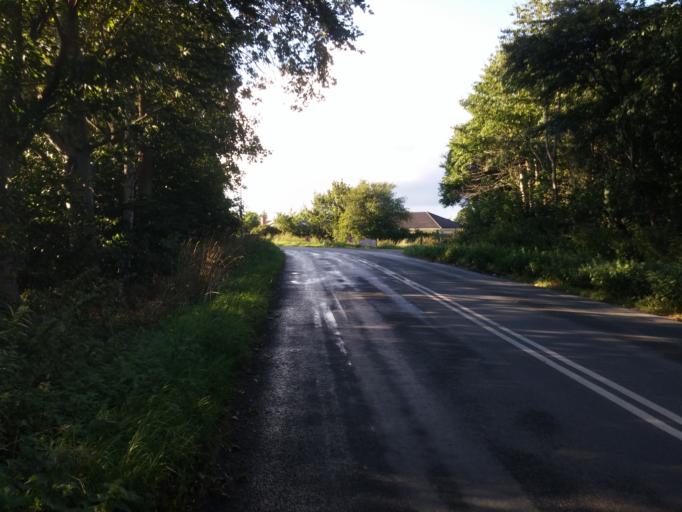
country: DK
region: Zealand
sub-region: Kalundborg Kommune
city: Svebolle
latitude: 55.7493
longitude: 11.3385
